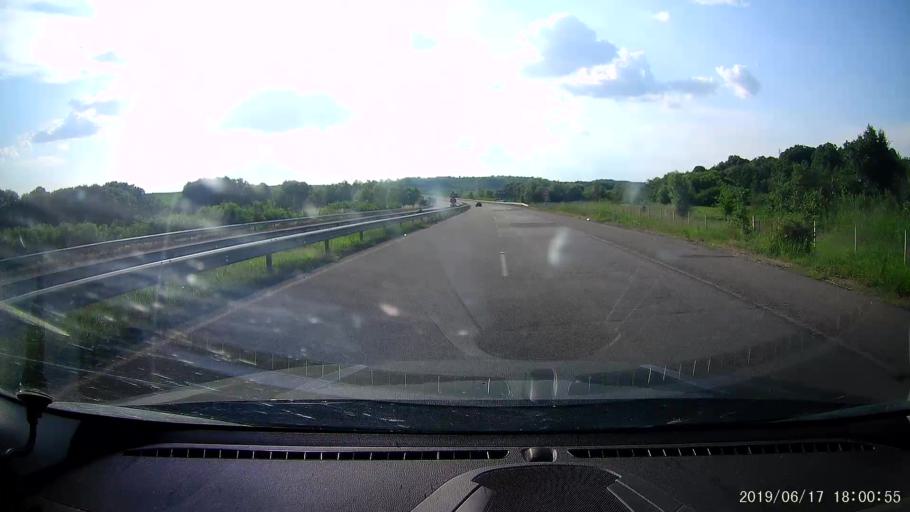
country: BG
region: Khaskovo
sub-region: Obshtina Svilengrad
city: Svilengrad
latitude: 41.7418
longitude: 26.2692
